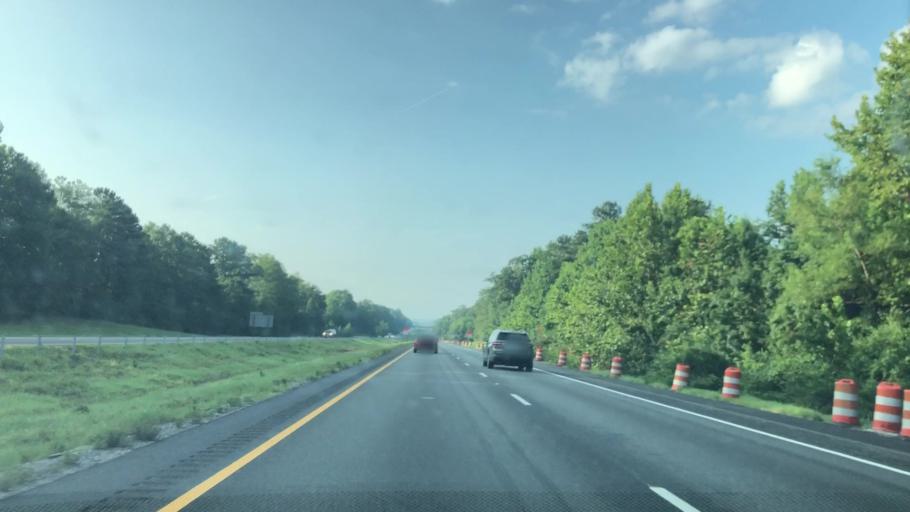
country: US
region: Alabama
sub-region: Chilton County
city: Clanton
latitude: 32.8319
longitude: -86.5913
